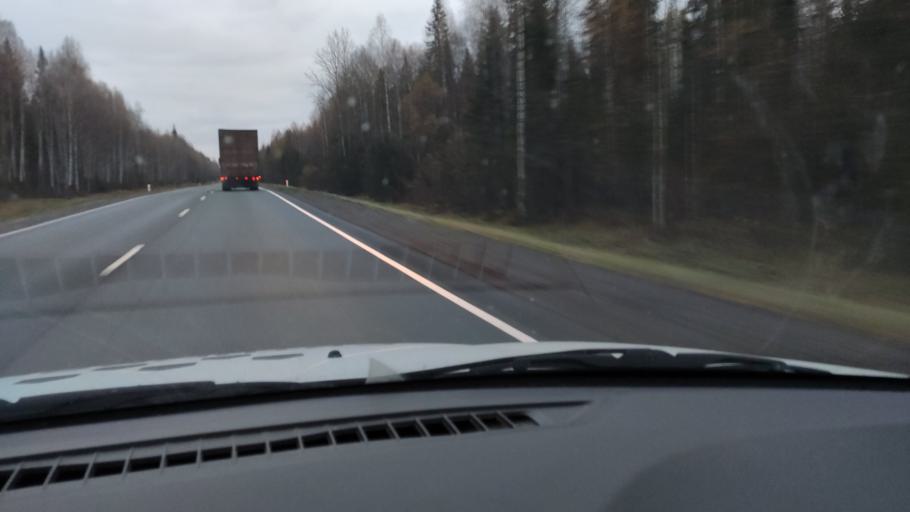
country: RU
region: Kirov
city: Kostino
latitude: 58.8358
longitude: 53.0470
